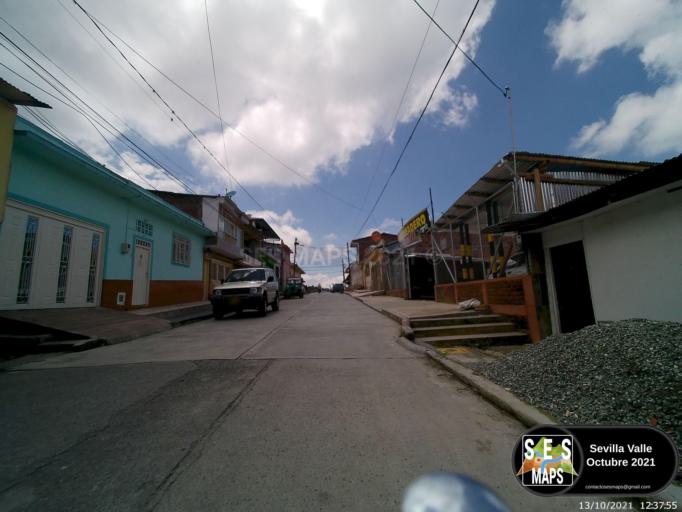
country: CO
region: Valle del Cauca
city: Sevilla
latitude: 4.2663
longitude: -75.9308
